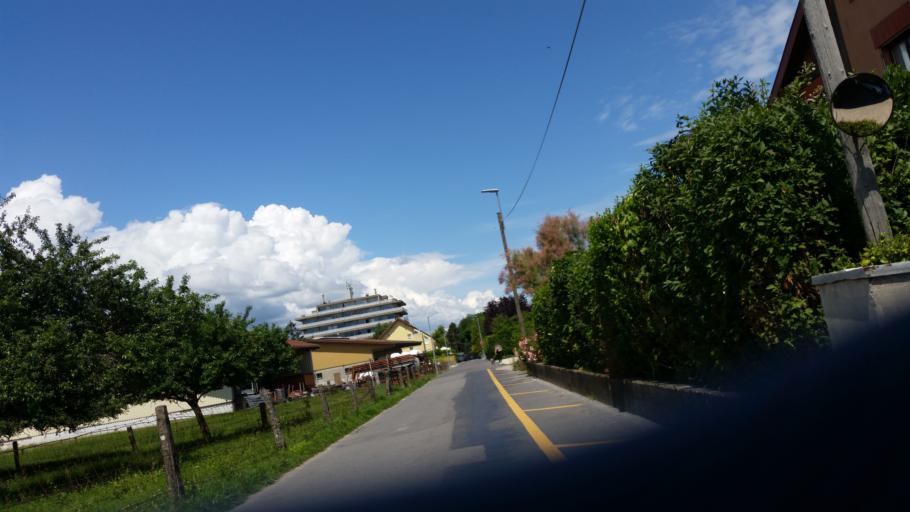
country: CH
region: Vaud
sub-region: Jura-Nord vaudois District
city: Yverdon-les-Bains
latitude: 46.7707
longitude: 6.6403
